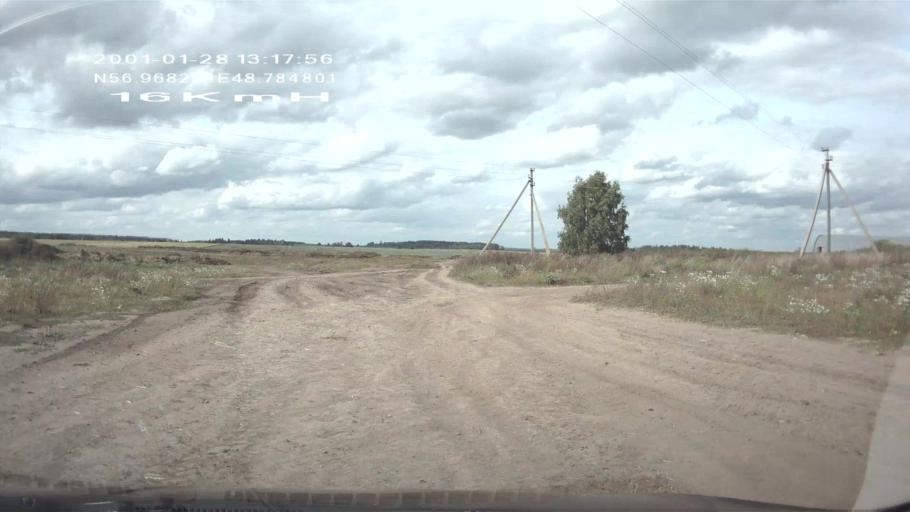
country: RU
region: Mariy-El
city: Kuzhener
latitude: 56.9683
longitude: 48.7847
